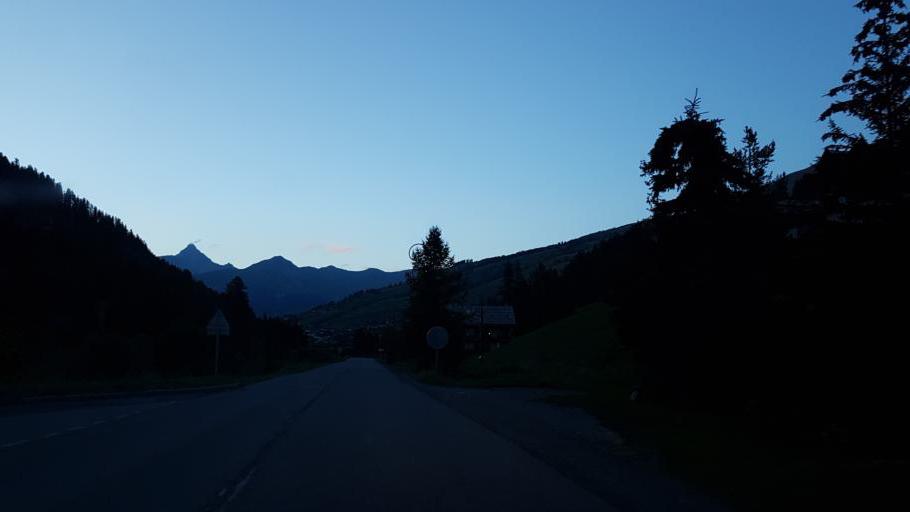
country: IT
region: Piedmont
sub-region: Provincia di Cuneo
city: Pontechianale
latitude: 44.7119
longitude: 6.8489
